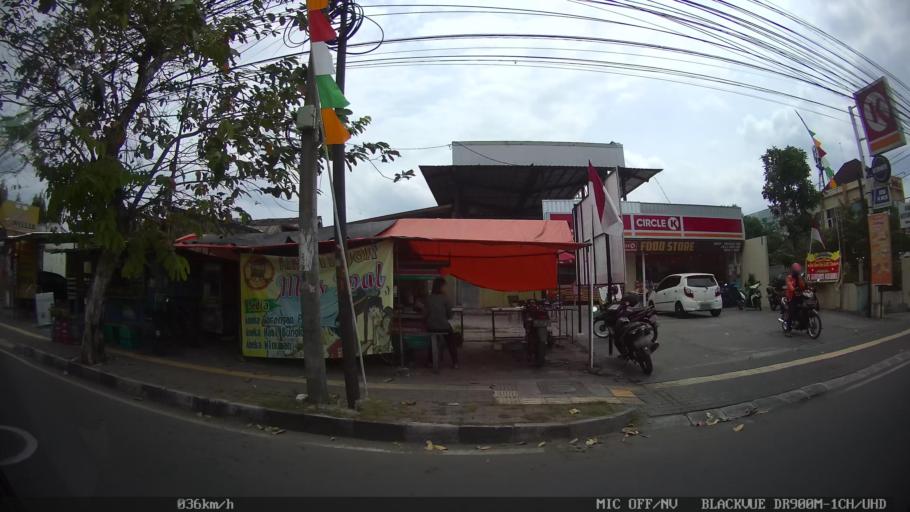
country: ID
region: Daerah Istimewa Yogyakarta
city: Yogyakarta
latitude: -7.7902
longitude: 110.3935
